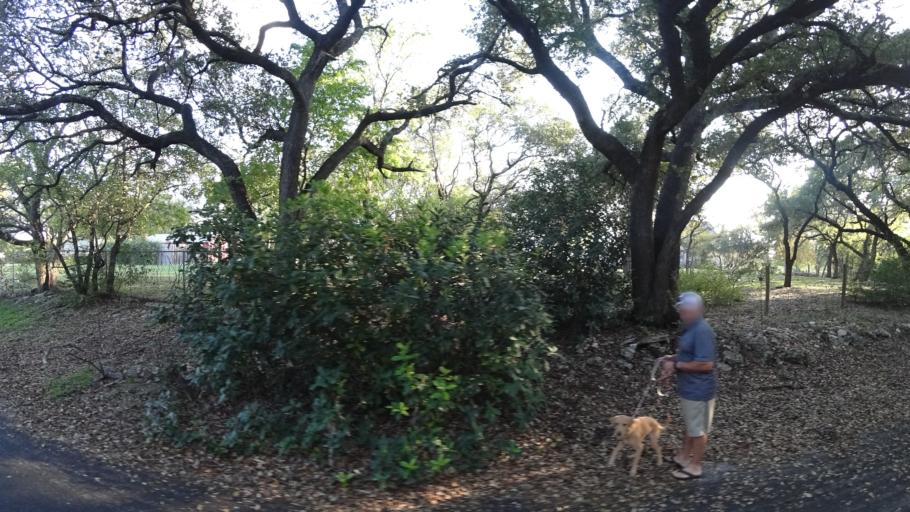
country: US
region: Texas
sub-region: Travis County
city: Lost Creek
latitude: 30.2968
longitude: -97.8454
